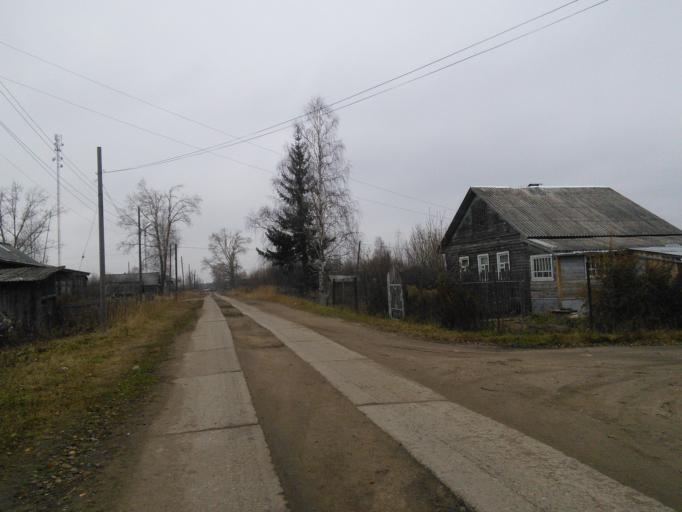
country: RU
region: Vologda
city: Kharovsk
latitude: 59.8089
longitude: 40.1738
